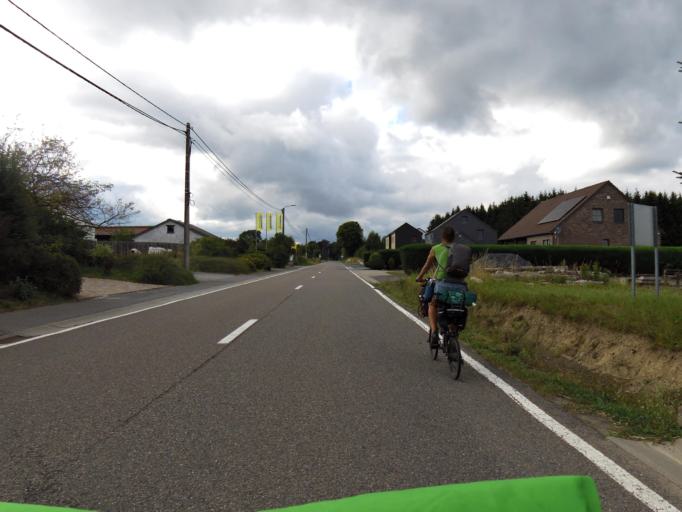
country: BE
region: Wallonia
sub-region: Province de Namur
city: Bievre
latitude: 49.9360
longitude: 5.0305
